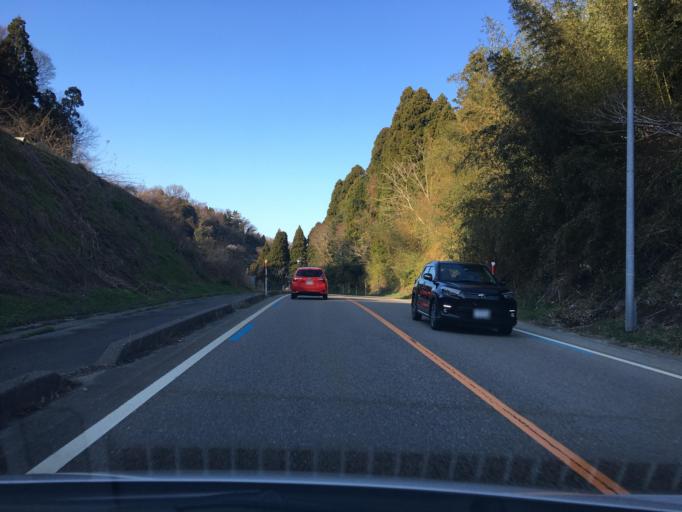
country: JP
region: Toyama
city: Himi
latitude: 36.9252
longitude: 137.0257
